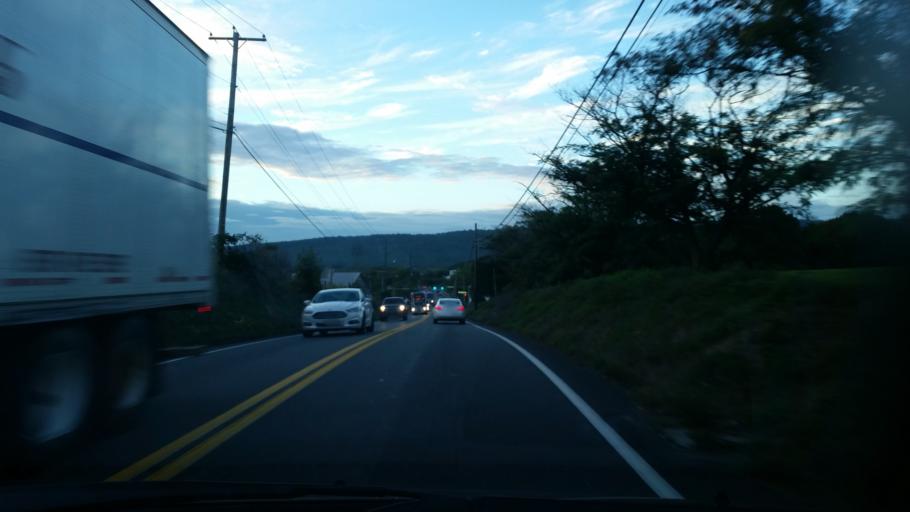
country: US
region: Pennsylvania
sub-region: Dauphin County
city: Skyline View
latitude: 40.3738
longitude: -76.6517
